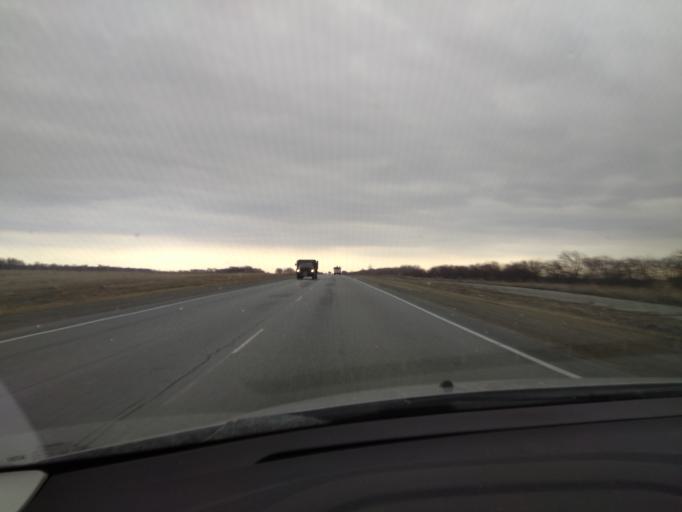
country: RU
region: Chelyabinsk
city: Tyubuk
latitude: 55.8403
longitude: 61.1771
